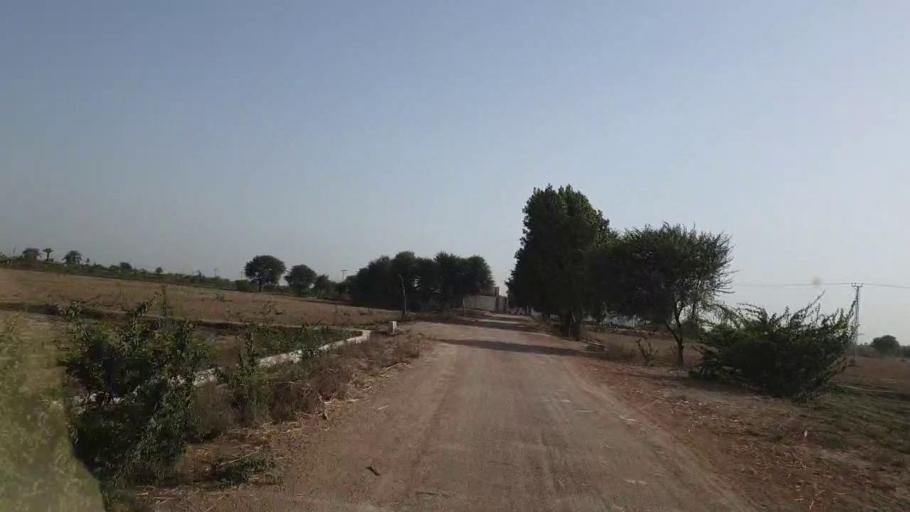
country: PK
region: Sindh
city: Tando Ghulam Ali
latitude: 25.0867
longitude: 68.8530
